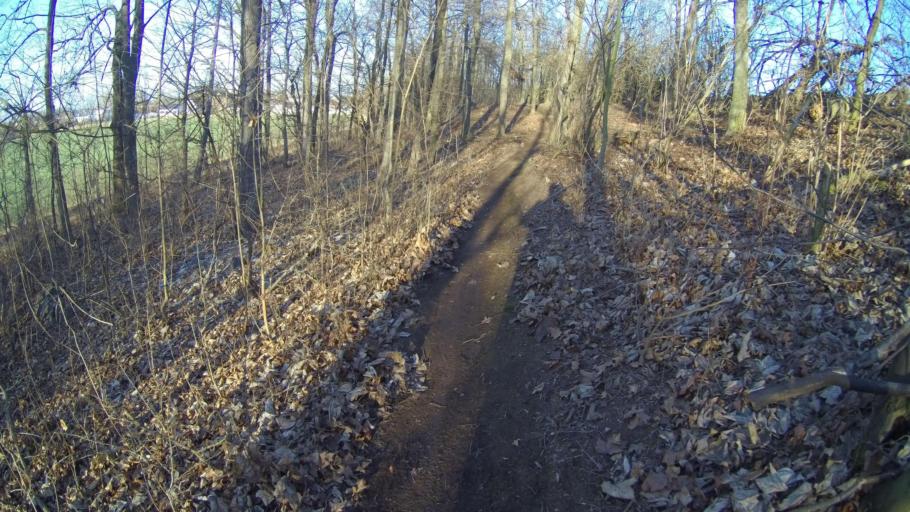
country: CZ
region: Central Bohemia
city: Neratovice
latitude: 50.2341
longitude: 14.5060
